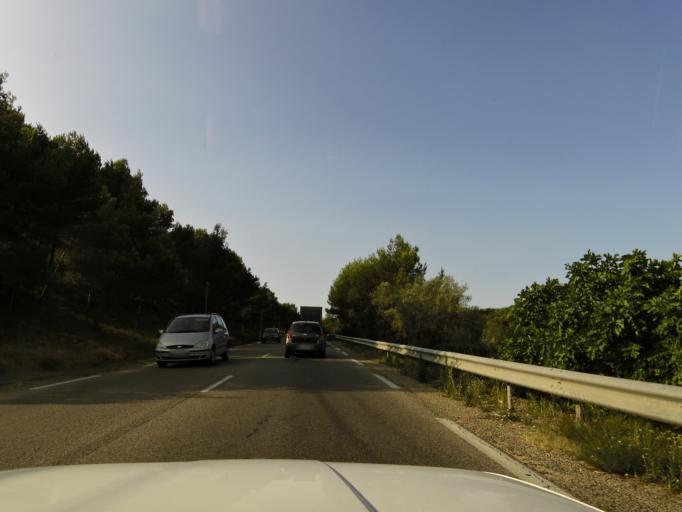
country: FR
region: Languedoc-Roussillon
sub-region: Departement du Gard
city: Saint-Nazaire
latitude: 44.2073
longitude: 4.6298
